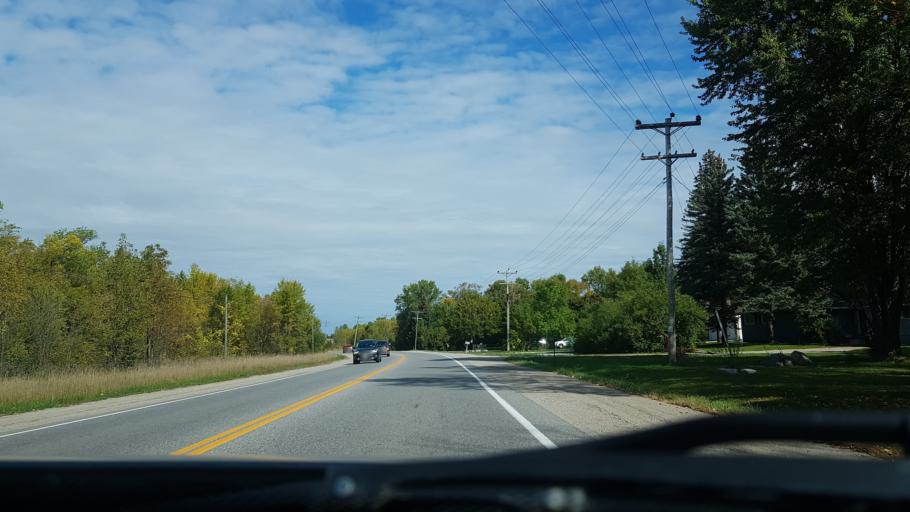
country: CA
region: Ontario
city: Orillia
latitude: 44.6183
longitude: -79.3529
